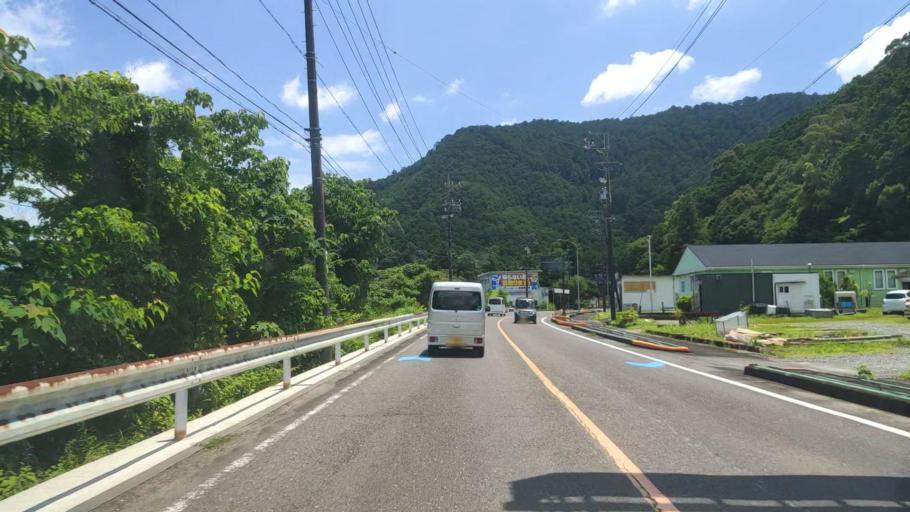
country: JP
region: Mie
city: Owase
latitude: 34.1180
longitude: 136.2195
